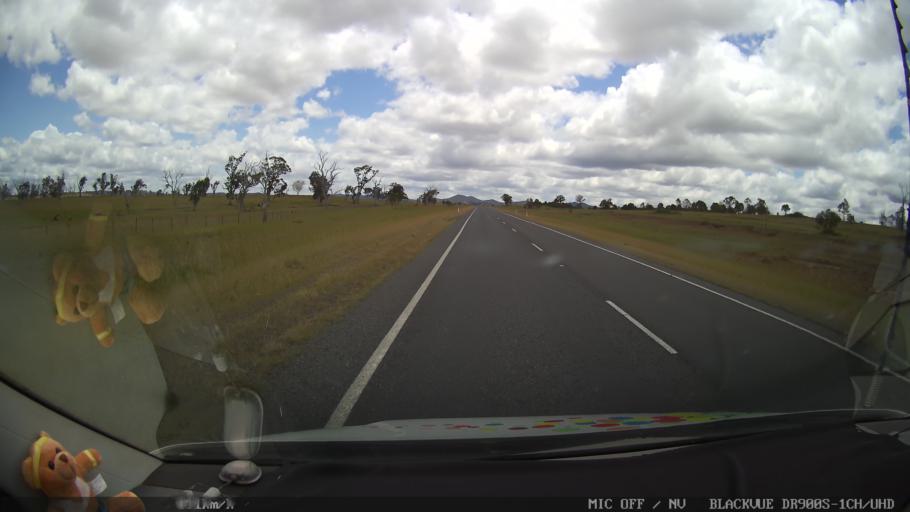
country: AU
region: New South Wales
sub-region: Glen Innes Severn
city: Glen Innes
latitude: -29.4082
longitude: 151.8697
